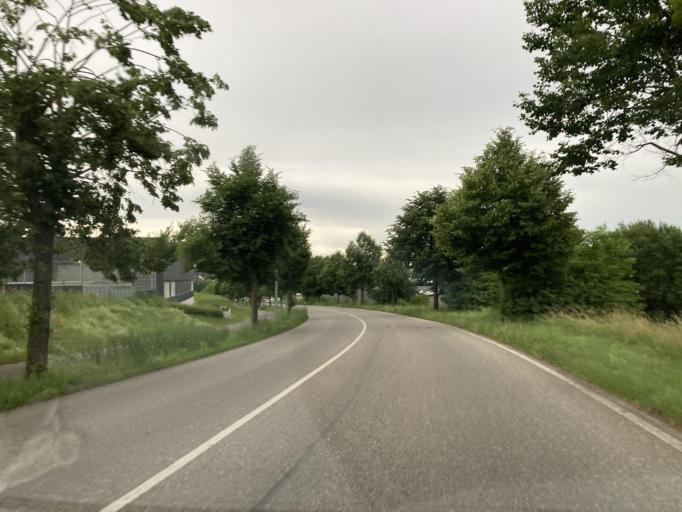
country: DE
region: Baden-Wuerttemberg
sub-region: Karlsruhe Region
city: Oberderdingen
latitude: 49.0809
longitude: 8.7732
